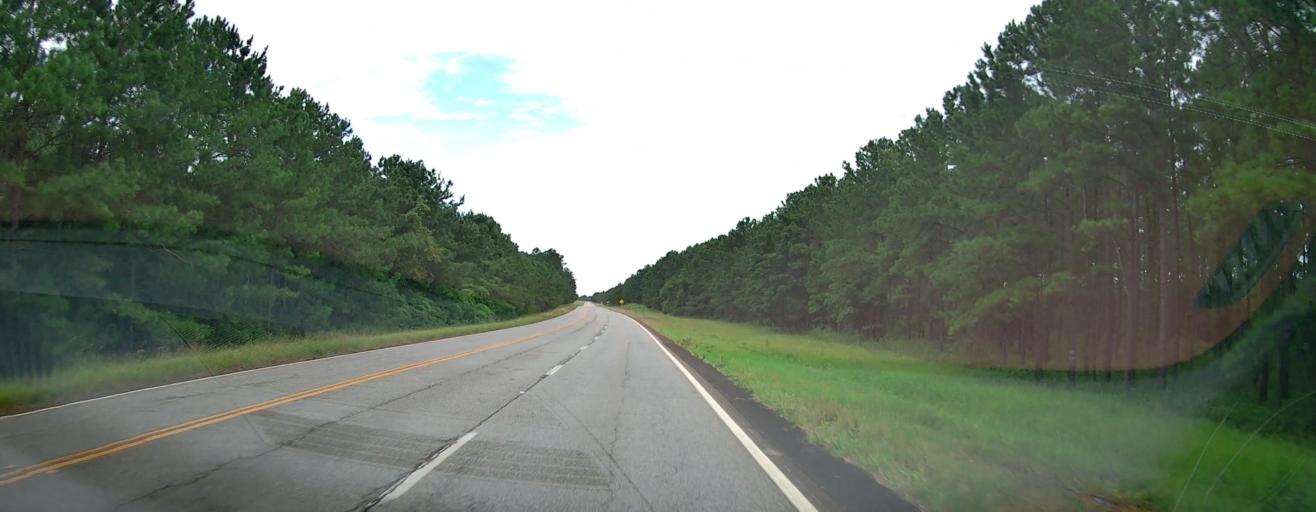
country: US
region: Georgia
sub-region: Marion County
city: Buena Vista
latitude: 32.2899
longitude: -84.4513
